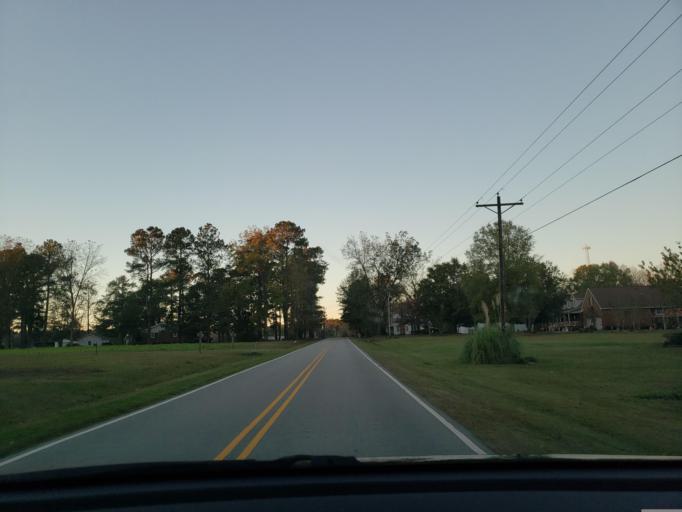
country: US
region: North Carolina
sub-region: Onslow County
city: Jacksonville
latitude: 34.7279
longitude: -77.5819
